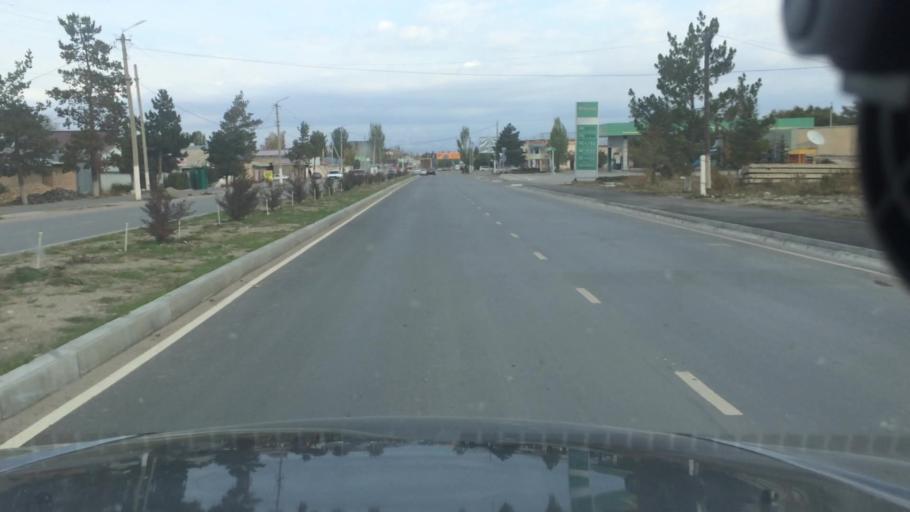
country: KG
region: Ysyk-Koel
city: Karakol
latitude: 42.5098
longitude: 78.3857
